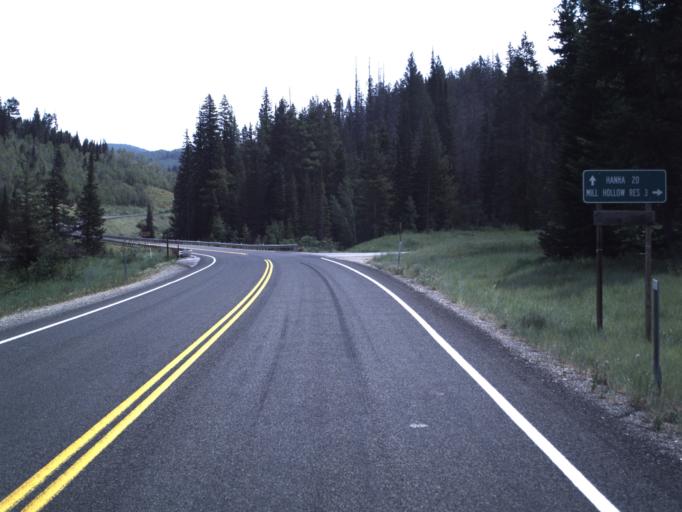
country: US
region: Utah
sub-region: Summit County
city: Francis
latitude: 40.5158
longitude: -111.0730
